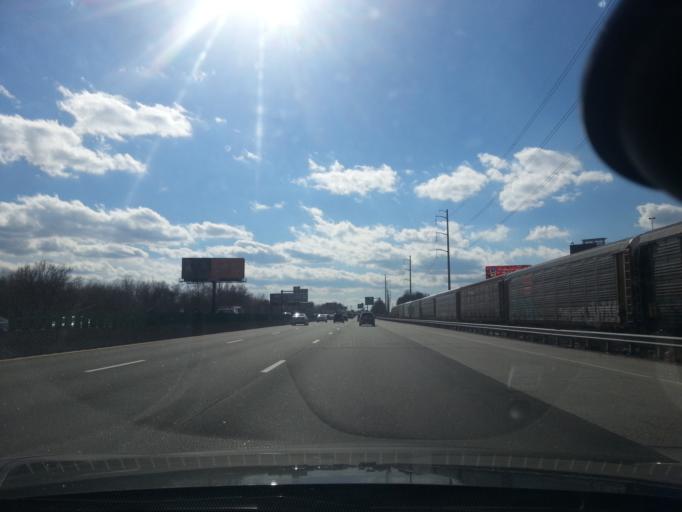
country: US
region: Pennsylvania
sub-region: Delaware County
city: Chester
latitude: 39.8546
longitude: -75.3671
